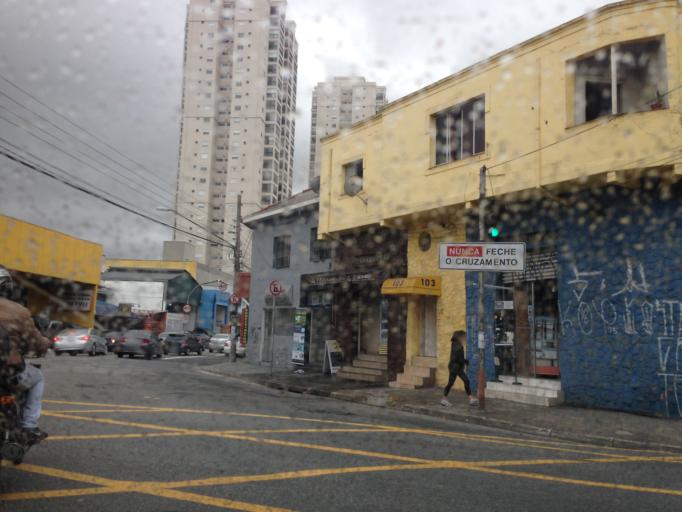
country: BR
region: Sao Paulo
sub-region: Sao Paulo
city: Sao Paulo
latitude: -23.5259
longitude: -46.7021
